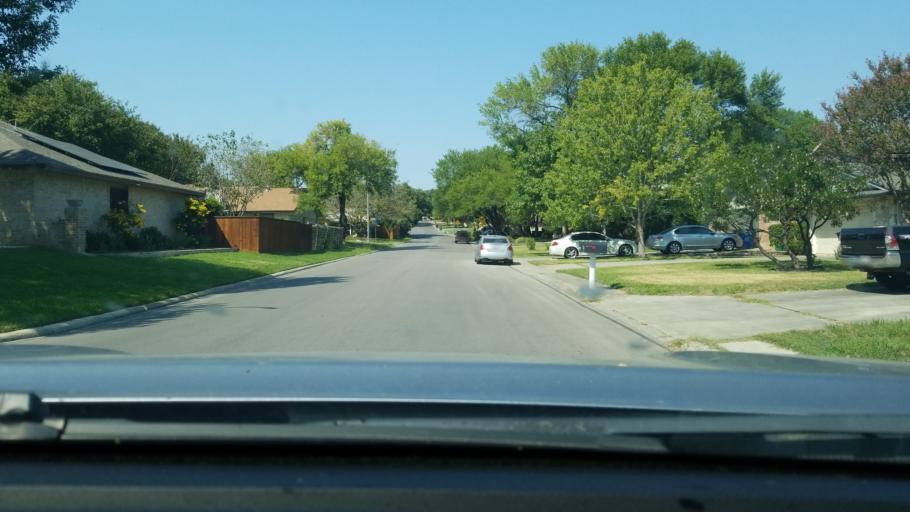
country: US
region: Texas
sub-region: Bexar County
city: Shavano Park
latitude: 29.5575
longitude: -98.6057
